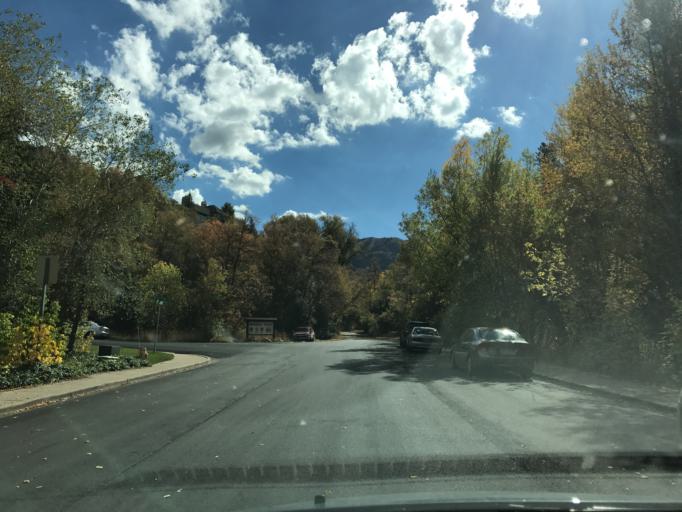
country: US
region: Utah
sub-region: Davis County
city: Bountiful
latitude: 40.8648
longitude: -111.8385
